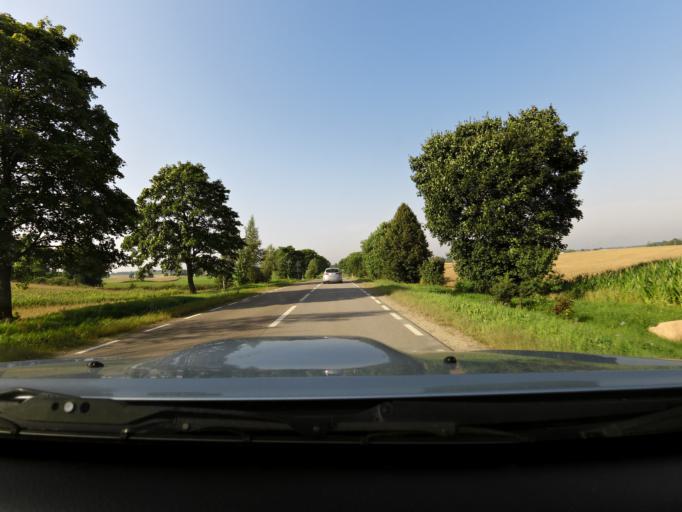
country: PL
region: Podlasie
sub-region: Powiat sejnenski
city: Sejny
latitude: 54.1033
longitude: 23.4055
